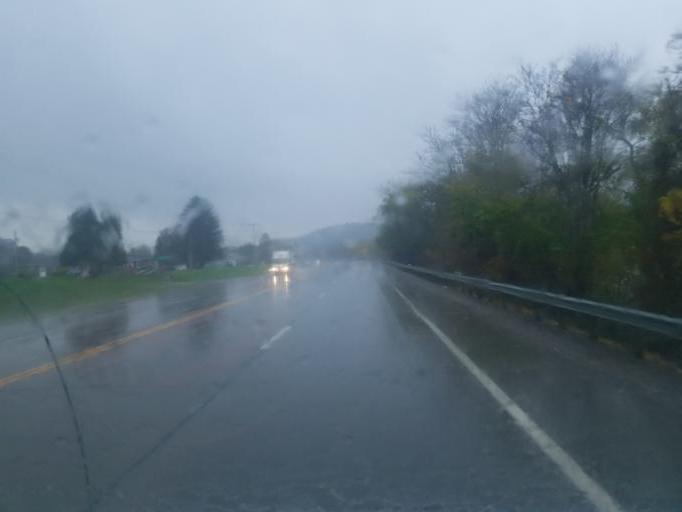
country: US
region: Ohio
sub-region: Muskingum County
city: South Zanesville
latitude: 39.9059
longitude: -82.0011
